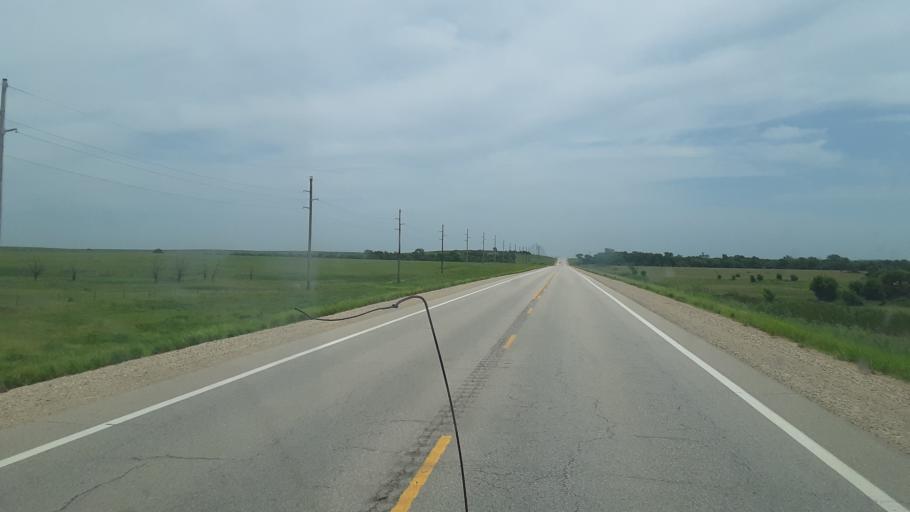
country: US
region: Kansas
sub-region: Greenwood County
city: Eureka
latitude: 37.8372
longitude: -96.0639
